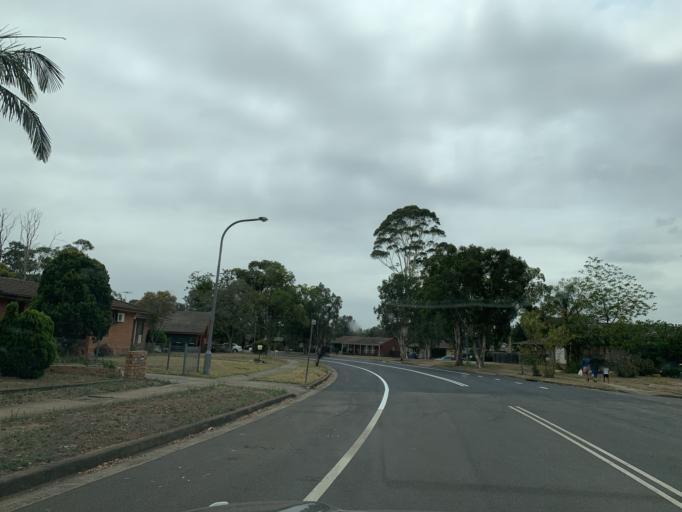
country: AU
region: New South Wales
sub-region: Blacktown
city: Doonside
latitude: -33.7524
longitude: 150.8748
